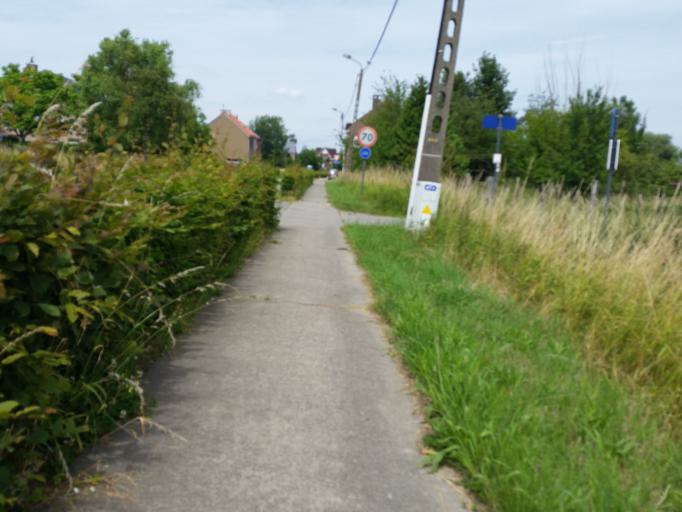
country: BE
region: Flanders
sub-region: Provincie Antwerpen
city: Rumst
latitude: 51.0445
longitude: 4.4136
